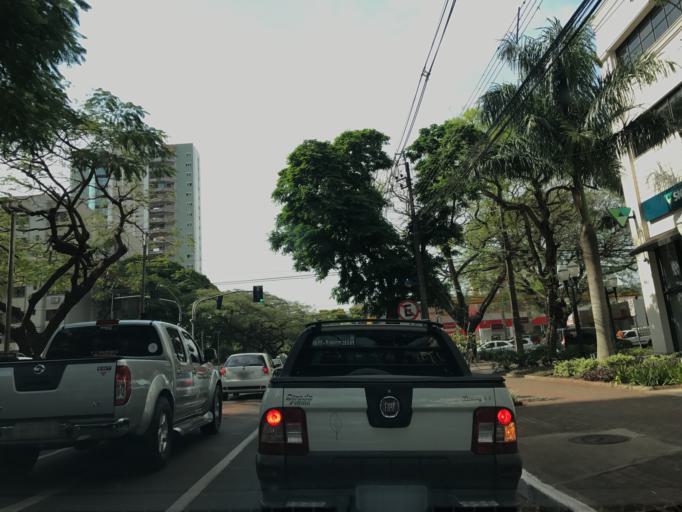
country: BR
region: Parana
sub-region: Maringa
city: Maringa
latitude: -23.4186
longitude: -51.9274
